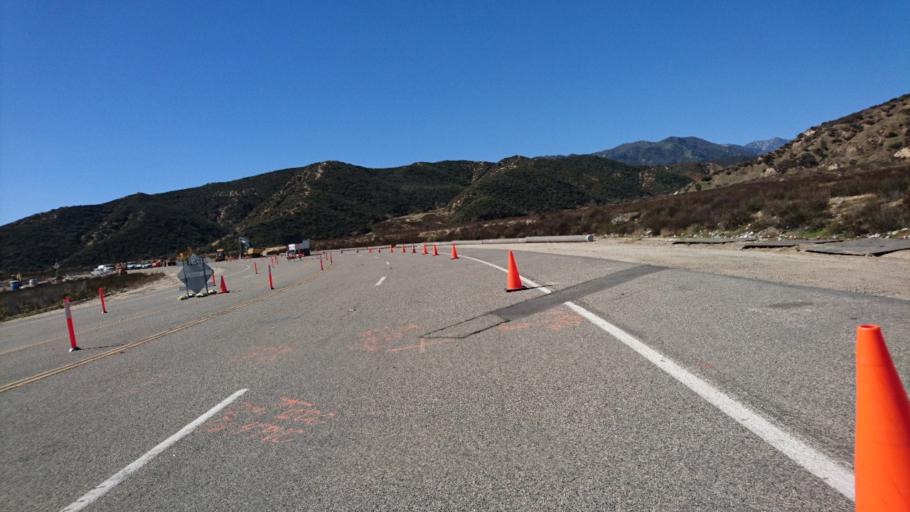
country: US
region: California
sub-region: San Bernardino County
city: Muscoy
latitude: 34.2029
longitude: -117.4165
